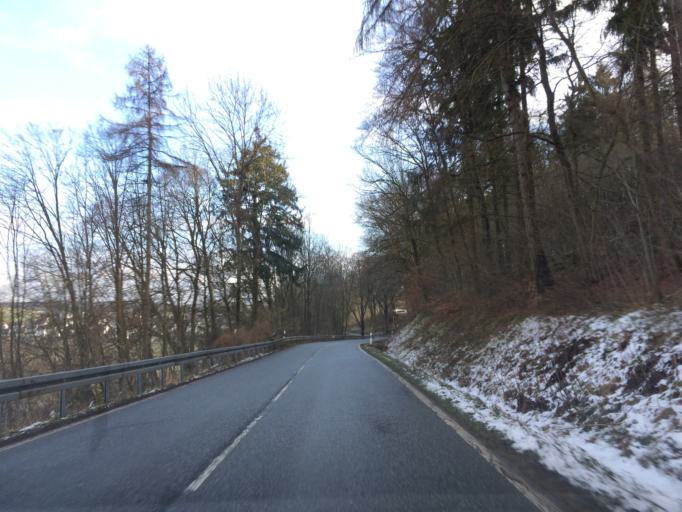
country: DE
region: Hesse
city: Bad Camberg
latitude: 50.3315
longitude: 8.3399
